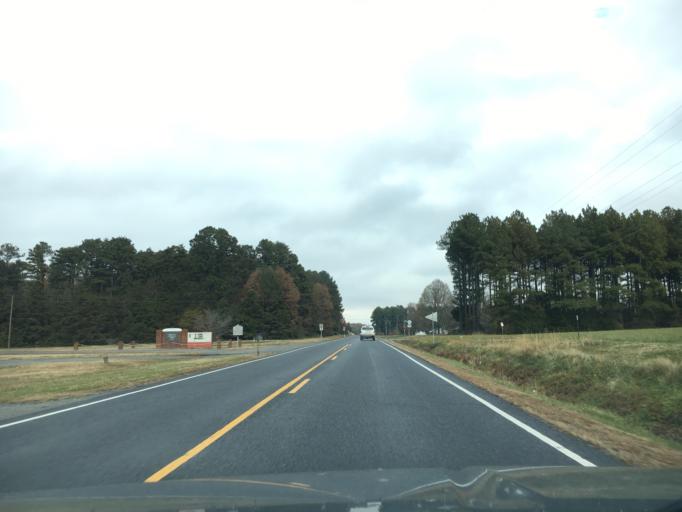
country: US
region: Virginia
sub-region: Prince Edward County
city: Farmville
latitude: 37.3451
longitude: -78.3856
